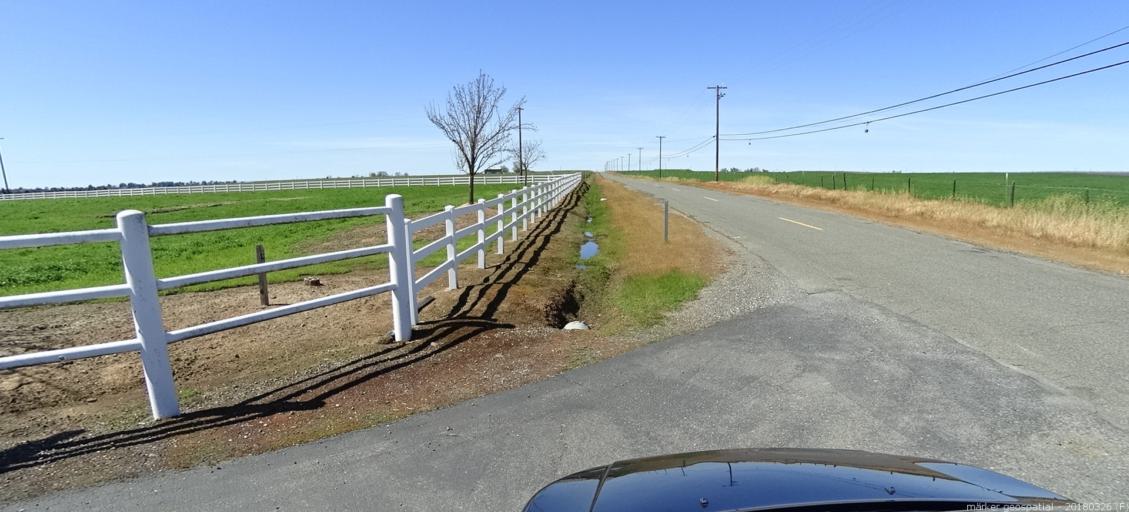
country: US
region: California
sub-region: Sacramento County
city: Wilton
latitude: 38.4677
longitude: -121.2482
